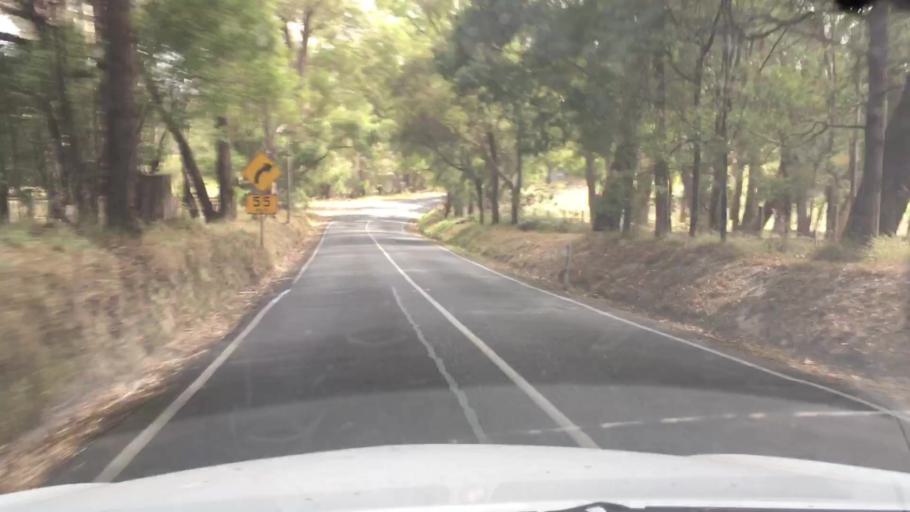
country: AU
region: Victoria
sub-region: Yarra Ranges
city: Macclesfield
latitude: -37.8275
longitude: 145.4901
